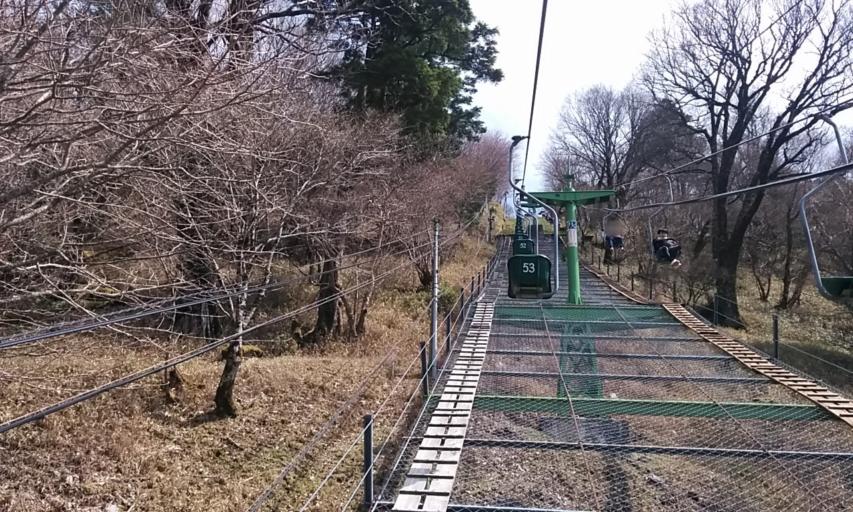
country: JP
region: Tokushima
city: Wakimachi
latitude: 33.8645
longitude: 134.0901
